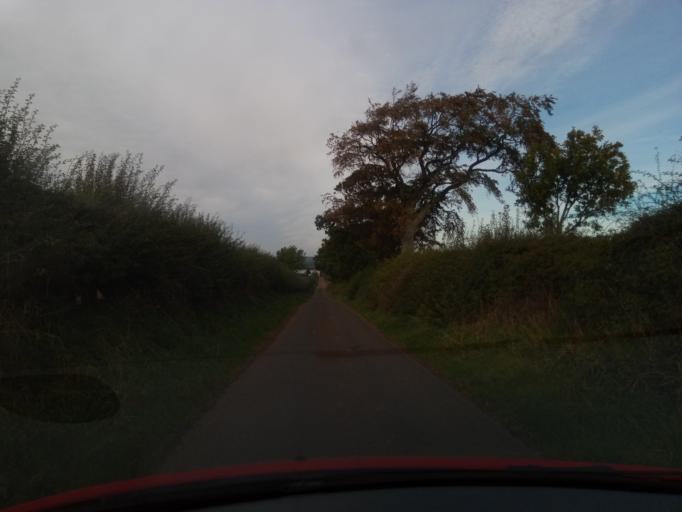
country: GB
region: Scotland
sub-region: The Scottish Borders
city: Kelso
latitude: 55.5918
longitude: -2.3855
